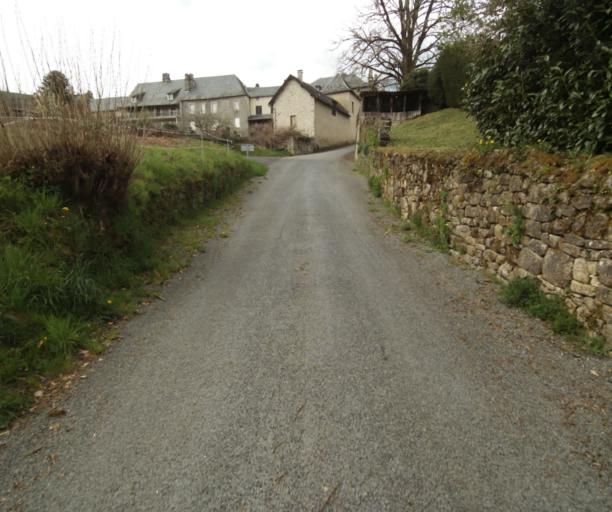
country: FR
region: Limousin
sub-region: Departement de la Correze
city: Argentat
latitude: 45.1951
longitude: 1.9710
